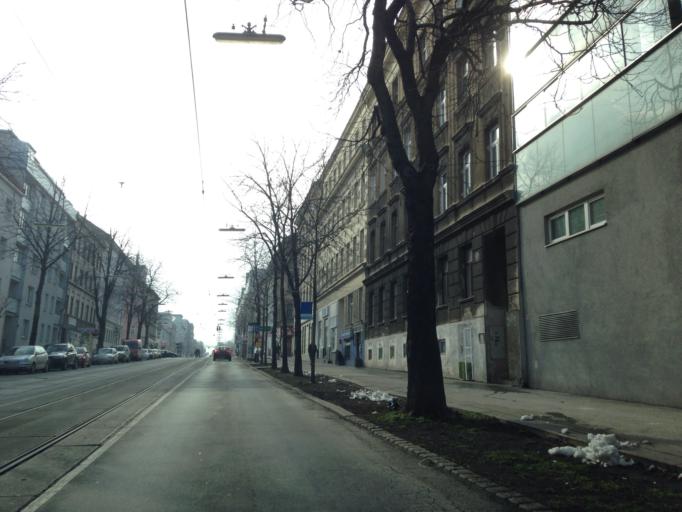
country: AT
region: Vienna
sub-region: Wien Stadt
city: Vienna
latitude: 48.2121
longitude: 16.3060
